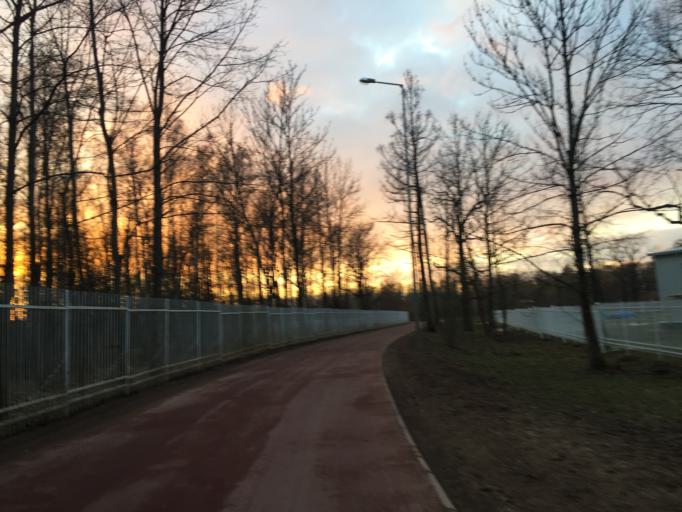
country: RU
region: St.-Petersburg
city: Pushkin
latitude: 59.7255
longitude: 30.3788
